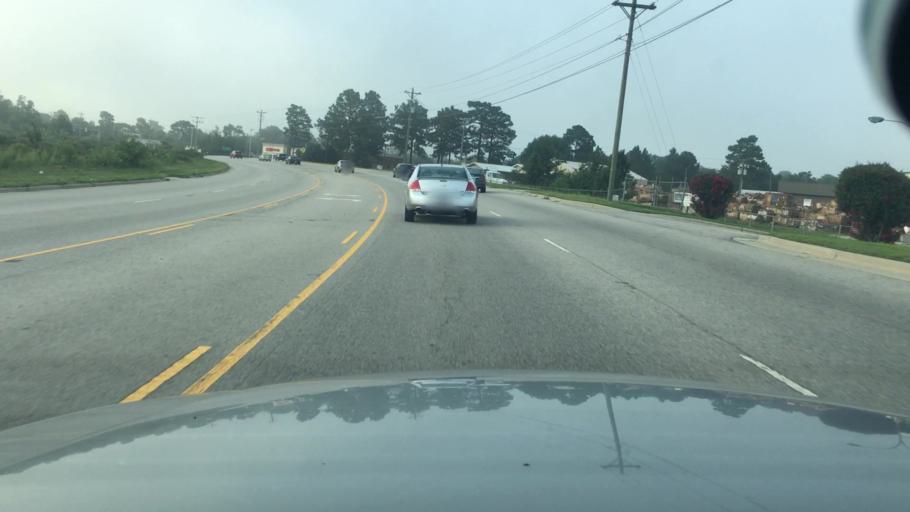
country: US
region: North Carolina
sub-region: Cumberland County
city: Hope Mills
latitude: 35.0061
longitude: -78.9185
